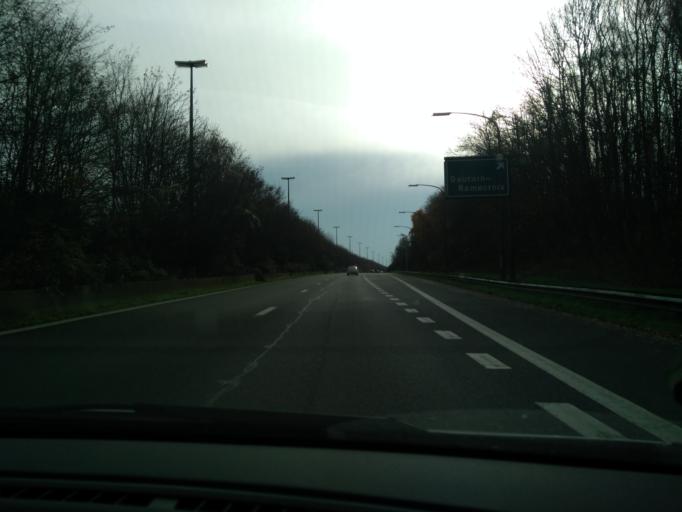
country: BE
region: Wallonia
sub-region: Province du Hainaut
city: Antoing
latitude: 50.5818
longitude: 3.4799
